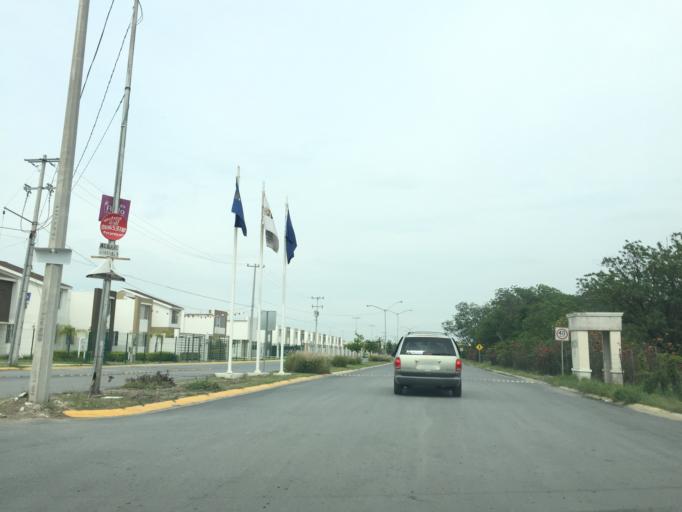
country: MX
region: Nuevo Leon
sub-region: Apodaca
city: Fraccionamiento Cosmopolis Octavo Sector
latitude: 25.8009
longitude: -100.2237
